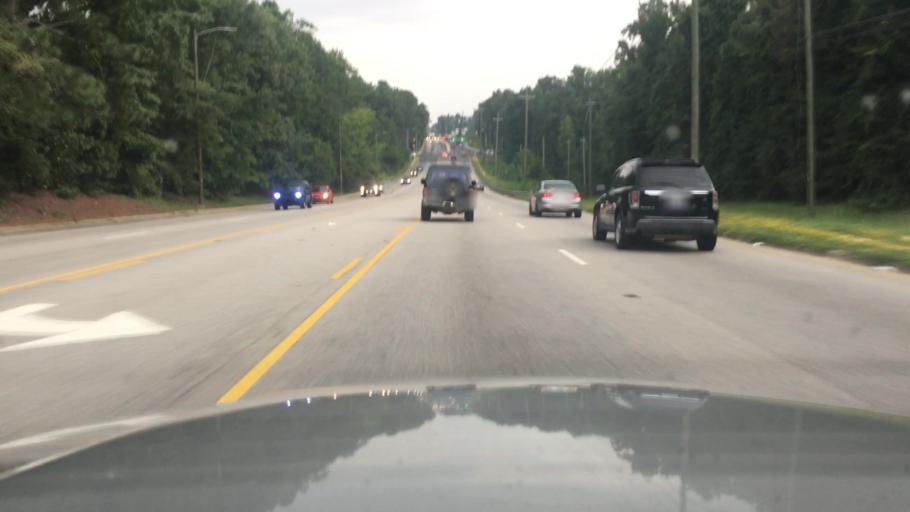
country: US
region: North Carolina
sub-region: Cumberland County
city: Fort Bragg
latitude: 35.0753
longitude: -79.0110
